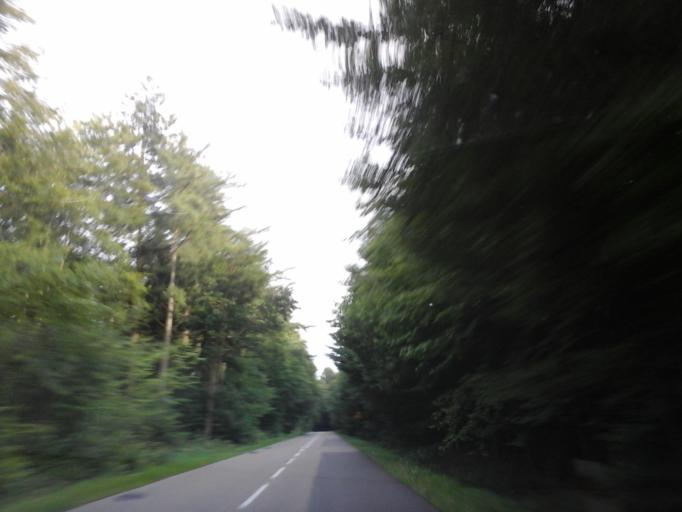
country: PL
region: West Pomeranian Voivodeship
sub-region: Powiat goleniowski
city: Nowogard
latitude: 53.7223
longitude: 15.0251
